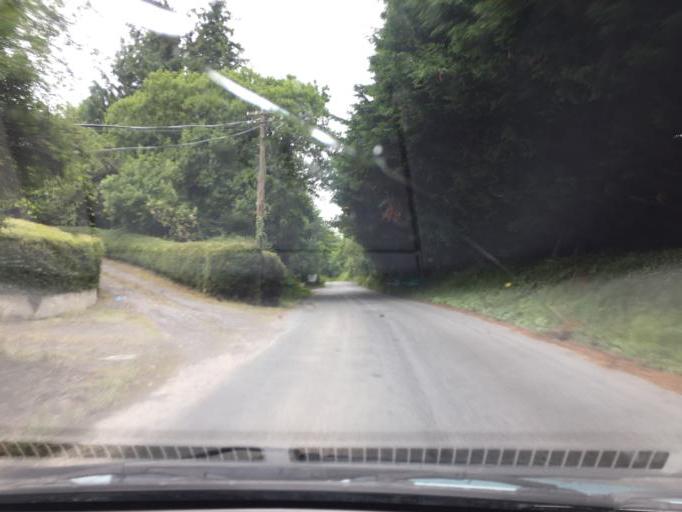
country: IE
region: Connaught
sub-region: Sligo
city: Sligo
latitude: 54.2373
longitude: -8.4502
